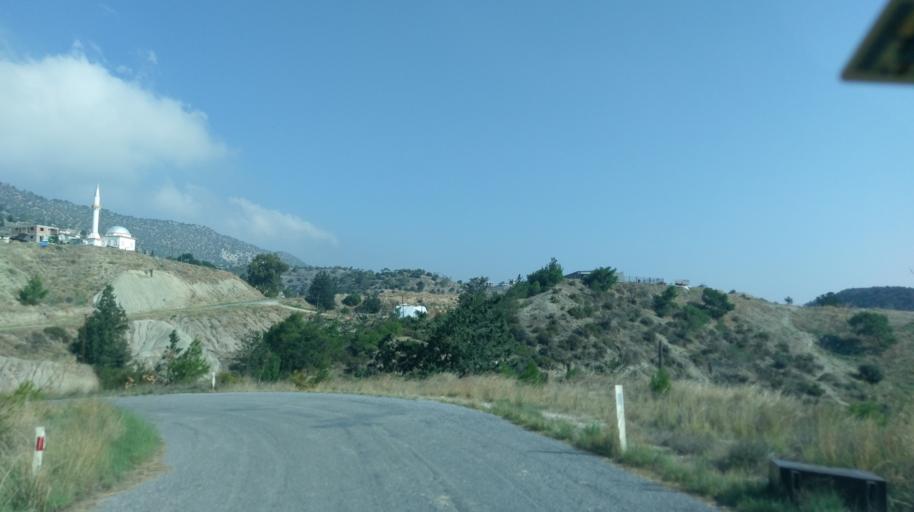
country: CY
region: Ammochostos
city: Lefkonoiko
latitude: 35.3254
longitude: 33.6768
